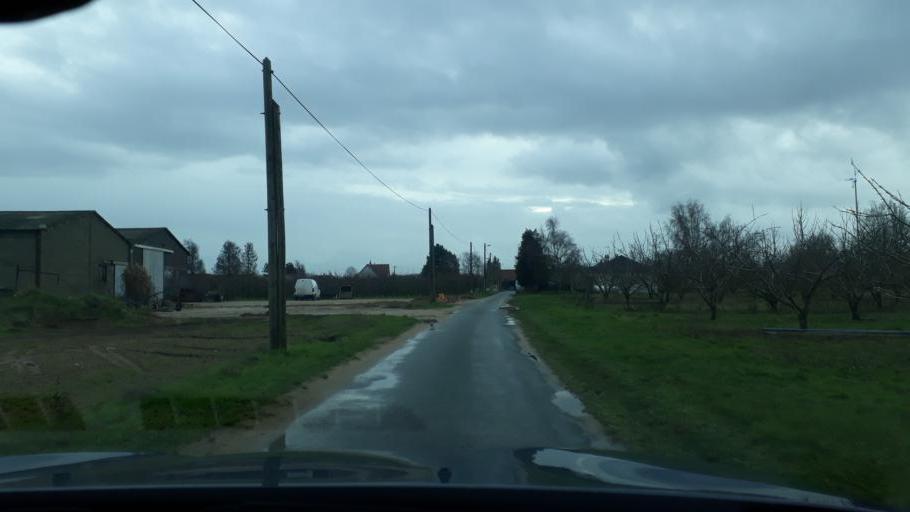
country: FR
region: Centre
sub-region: Departement du Loiret
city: Mareau-aux-Pres
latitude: 47.8316
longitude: 1.8015
